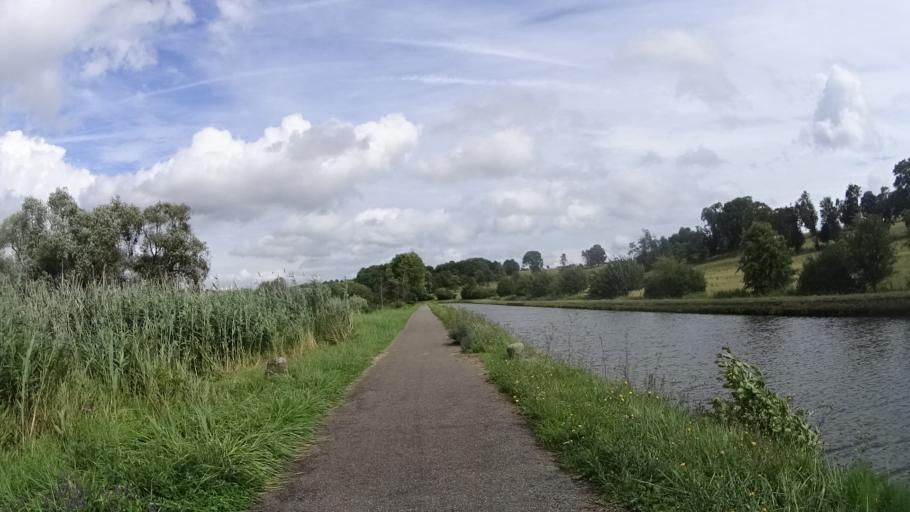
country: FR
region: Lorraine
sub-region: Departement de la Moselle
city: Lorquin
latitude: 48.6814
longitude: 6.9427
